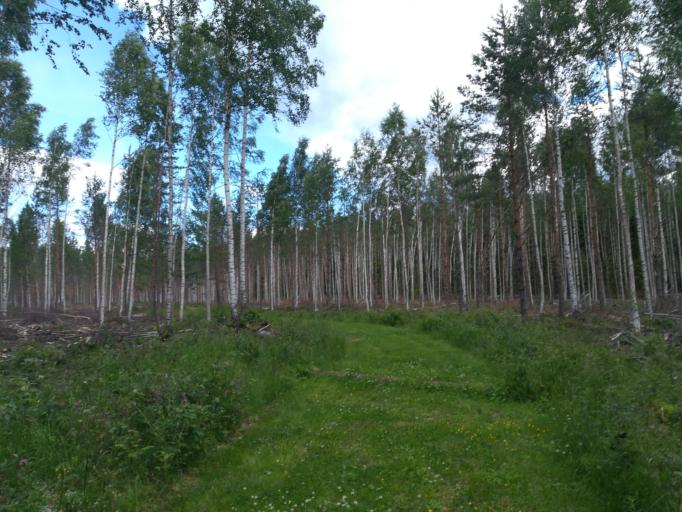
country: FI
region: Southern Savonia
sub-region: Mikkeli
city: Hirvensalmi
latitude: 61.6534
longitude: 26.7811
